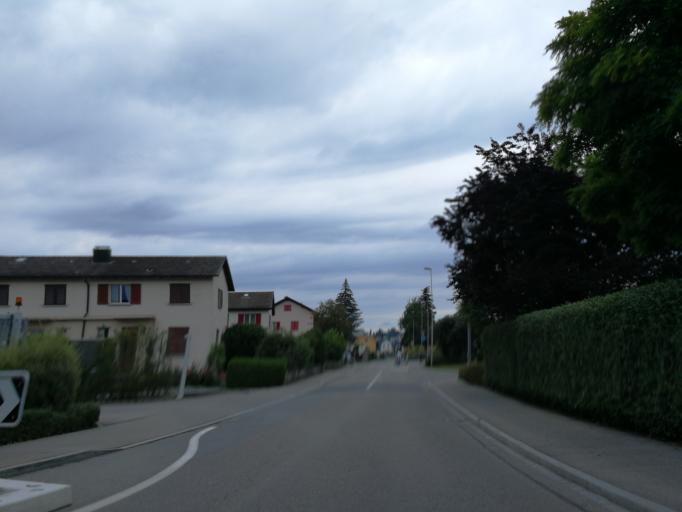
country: CH
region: Saint Gallen
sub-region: Wahlkreis See-Gaster
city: Jona
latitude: 47.2251
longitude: 8.8454
